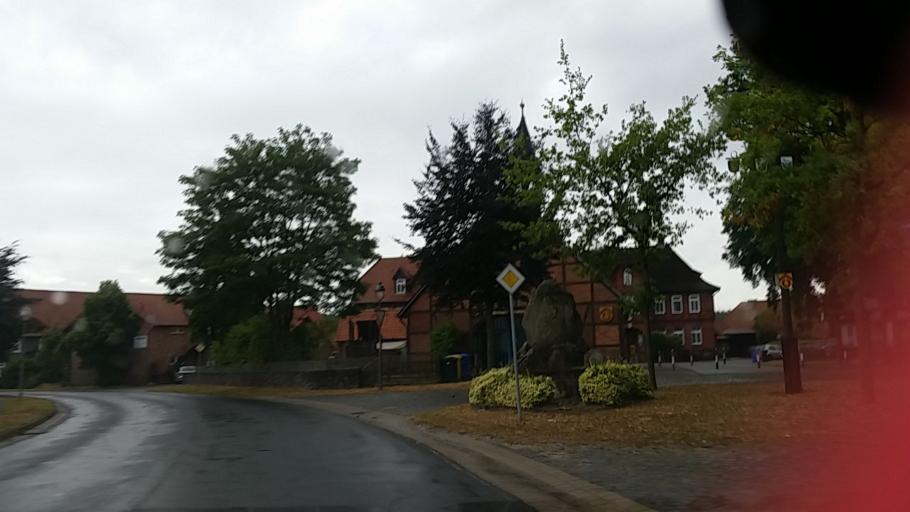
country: DE
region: Lower Saxony
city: Bokensdorf
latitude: 52.4969
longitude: 10.7131
